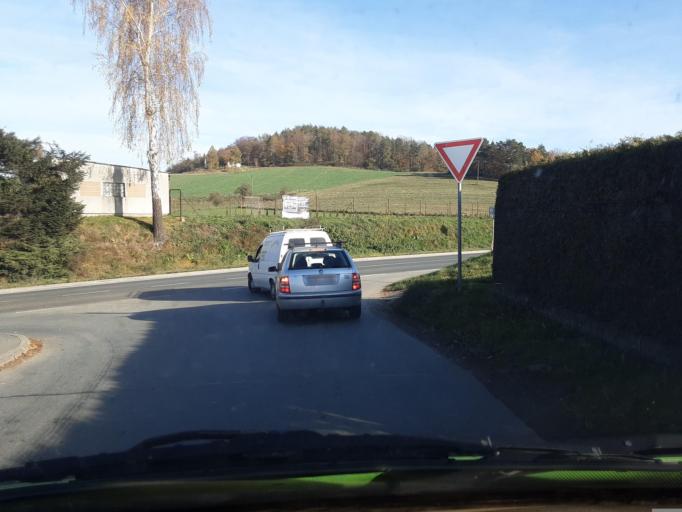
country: CZ
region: Plzensky
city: Klatovy
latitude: 49.3723
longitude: 13.3178
